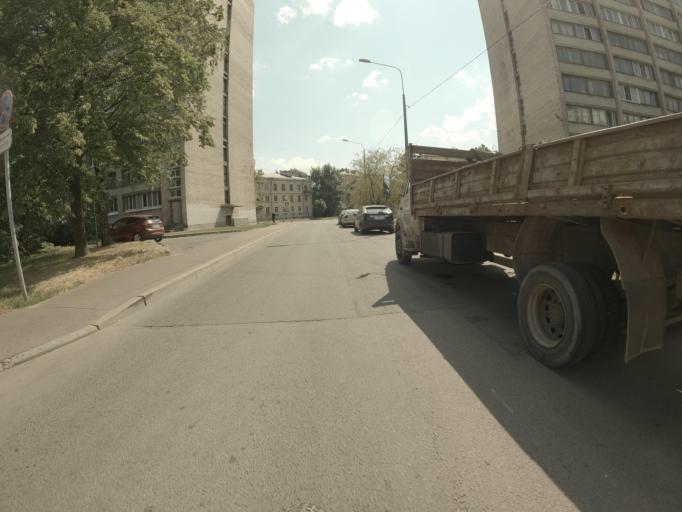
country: RU
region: St.-Petersburg
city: Avtovo
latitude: 59.8924
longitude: 30.2616
